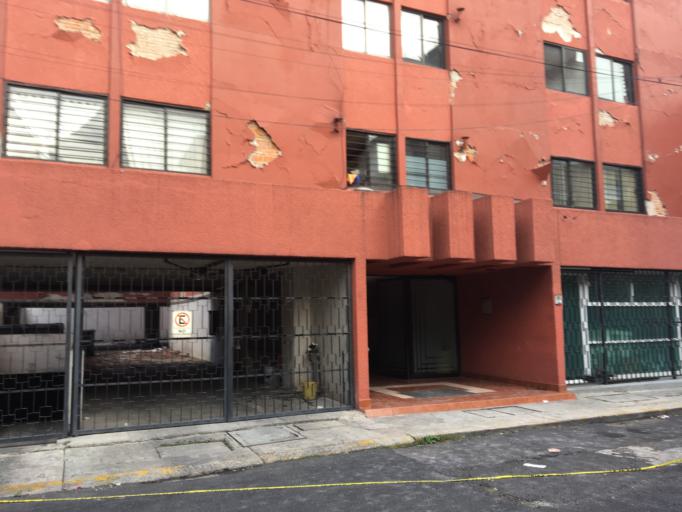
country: MX
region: Mexico City
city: Benito Juarez
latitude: 19.4053
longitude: -99.1637
